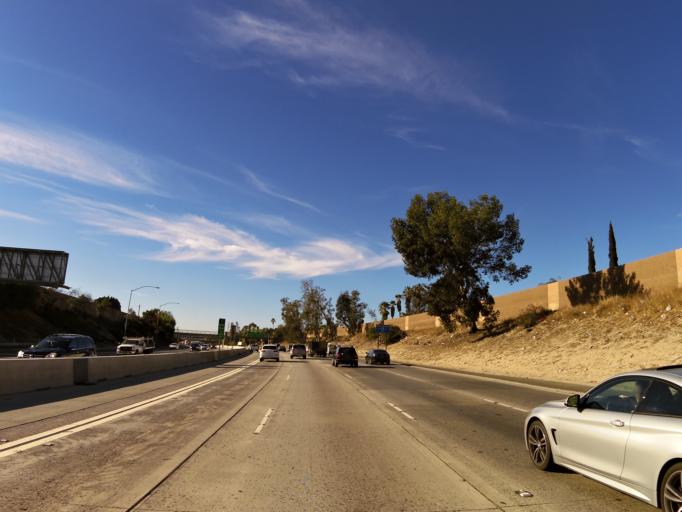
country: US
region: California
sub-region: Los Angeles County
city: North Hollywood
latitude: 34.2299
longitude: -118.3950
